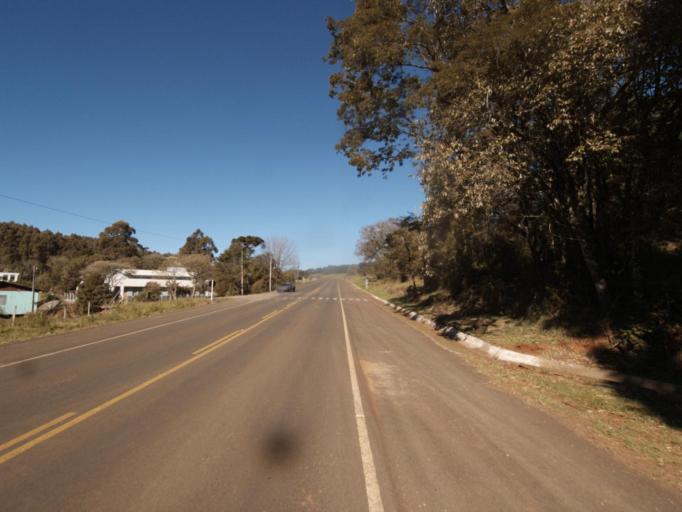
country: AR
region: Misiones
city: Bernardo de Irigoyen
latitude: -26.6777
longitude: -53.5609
